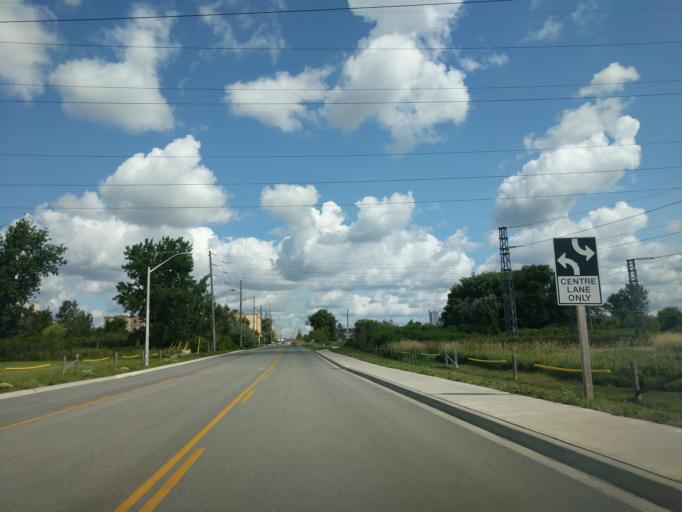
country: CA
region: Ontario
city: Scarborough
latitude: 43.8107
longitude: -79.2983
